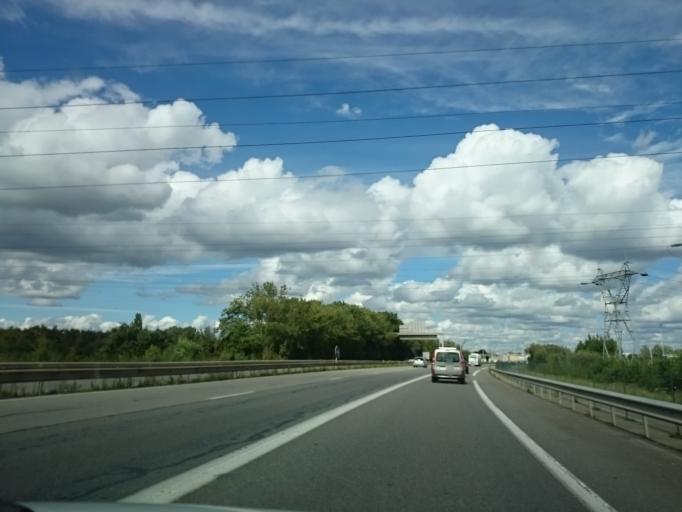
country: FR
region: Pays de la Loire
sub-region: Departement de la Loire-Atlantique
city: Bouguenais
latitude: 47.1828
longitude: -1.6054
